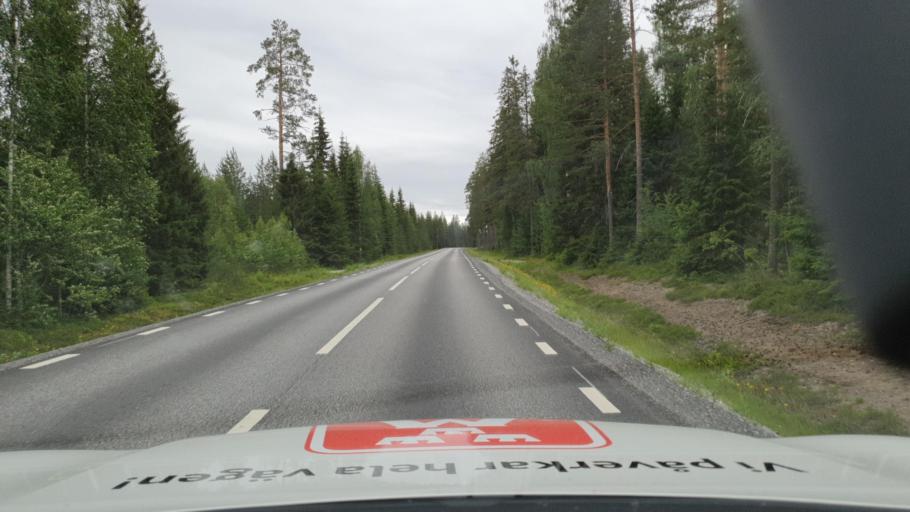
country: SE
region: Vaesterbotten
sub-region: Nordmalings Kommun
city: Nordmaling
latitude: 63.7106
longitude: 19.6331
